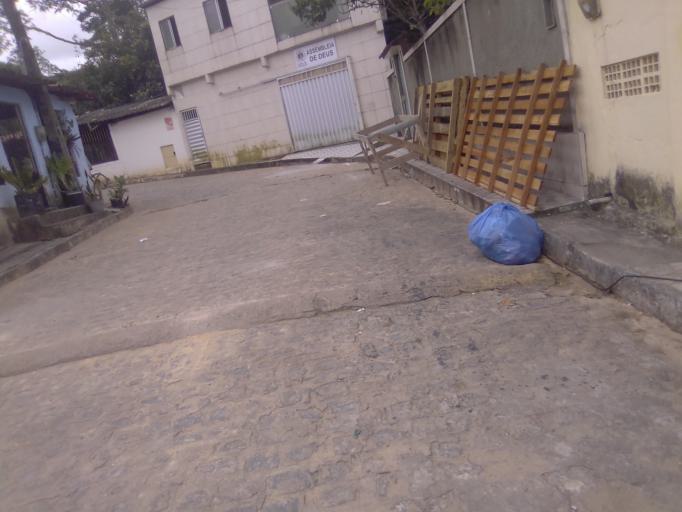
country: BR
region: Pernambuco
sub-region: Jaboatao Dos Guararapes
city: Jaboatao dos Guararapes
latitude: -8.0650
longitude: -35.0039
